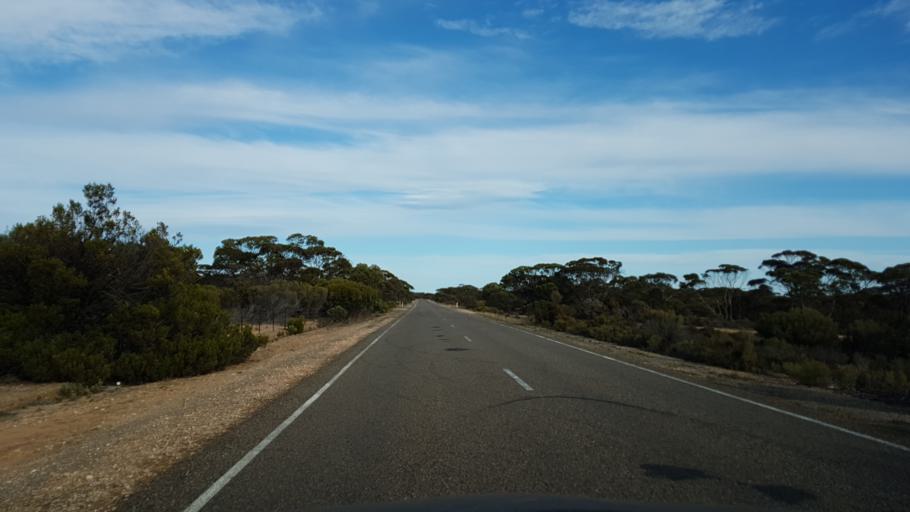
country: AU
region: South Australia
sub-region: Mid Murray
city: Mannum
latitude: -35.0105
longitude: 139.5191
